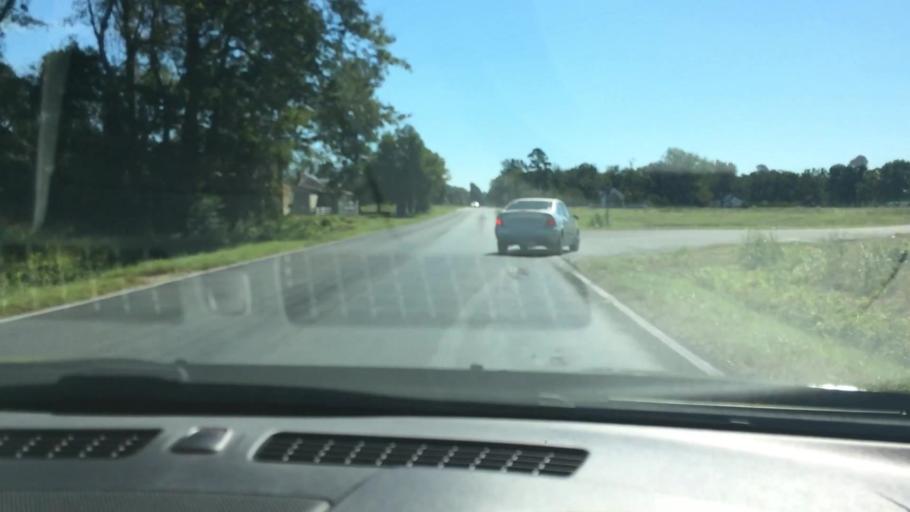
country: US
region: North Carolina
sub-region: Pitt County
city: Grifton
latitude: 35.3624
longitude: -77.3469
